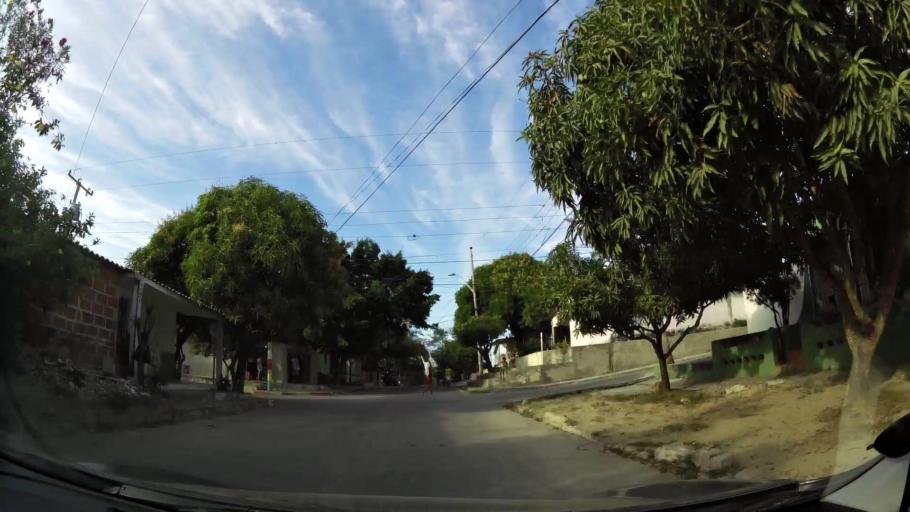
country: CO
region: Atlantico
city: Barranquilla
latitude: 10.9394
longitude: -74.8225
